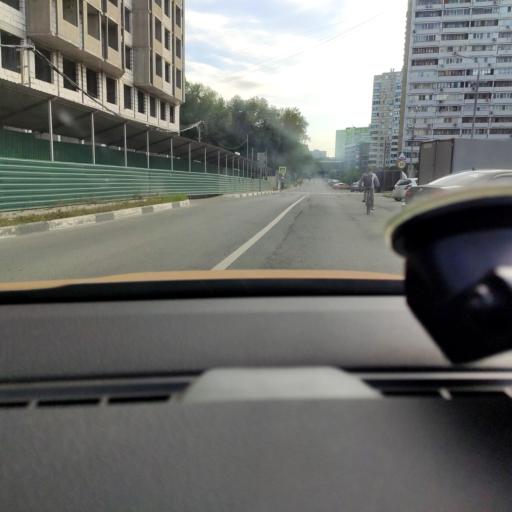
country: RU
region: Moskovskaya
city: Mytishchi
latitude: 55.9182
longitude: 37.7577
